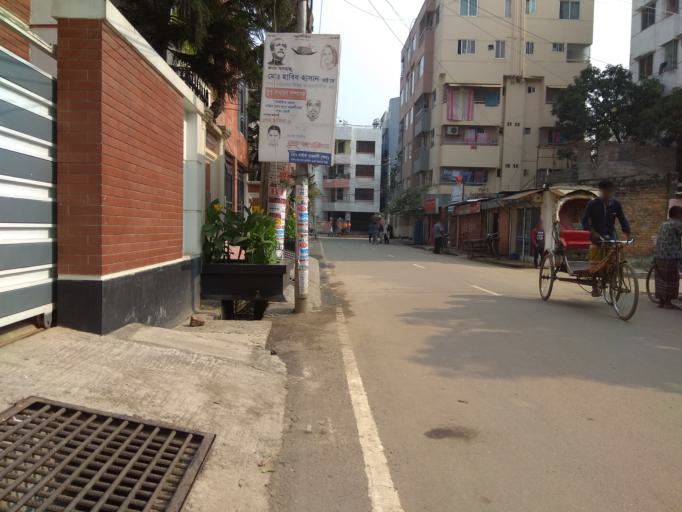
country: BD
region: Dhaka
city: Tungi
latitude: 23.8635
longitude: 90.3897
